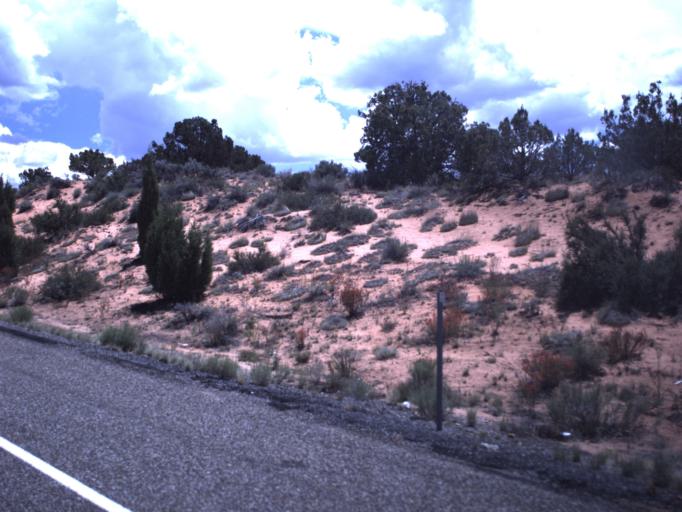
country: US
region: Utah
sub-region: Kane County
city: Kanab
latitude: 37.1810
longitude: -112.6384
